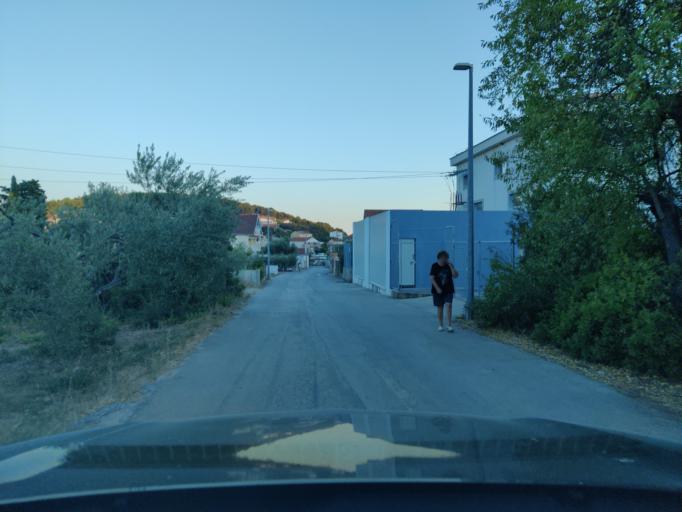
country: HR
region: Sibensko-Kniniska
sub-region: Grad Sibenik
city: Tisno
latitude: 43.8033
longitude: 15.6483
